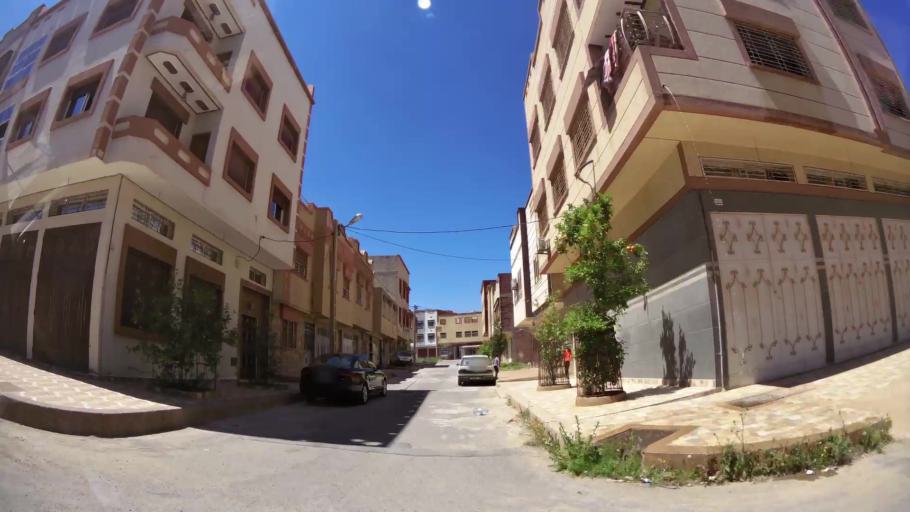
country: MA
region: Oriental
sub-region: Oujda-Angad
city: Oujda
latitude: 34.6608
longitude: -1.9479
